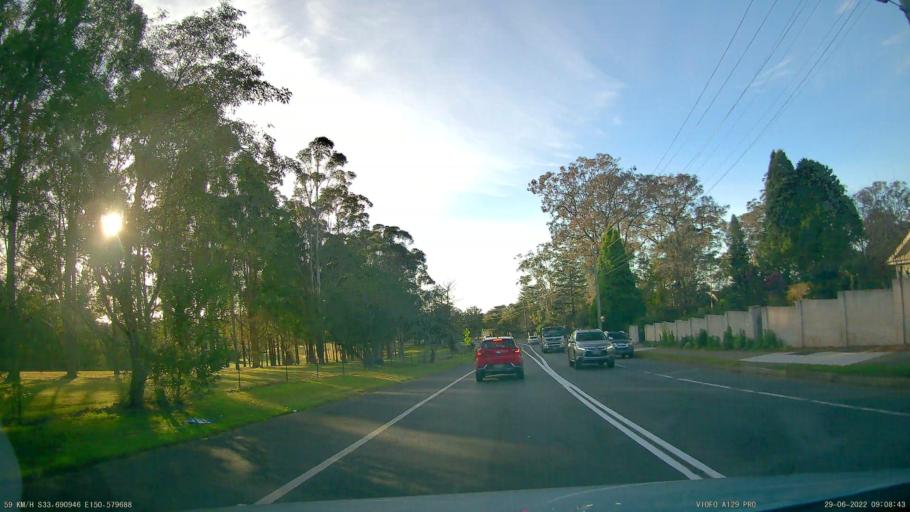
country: AU
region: New South Wales
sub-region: Blue Mountains Municipality
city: Blaxland
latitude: -33.6910
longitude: 150.5802
